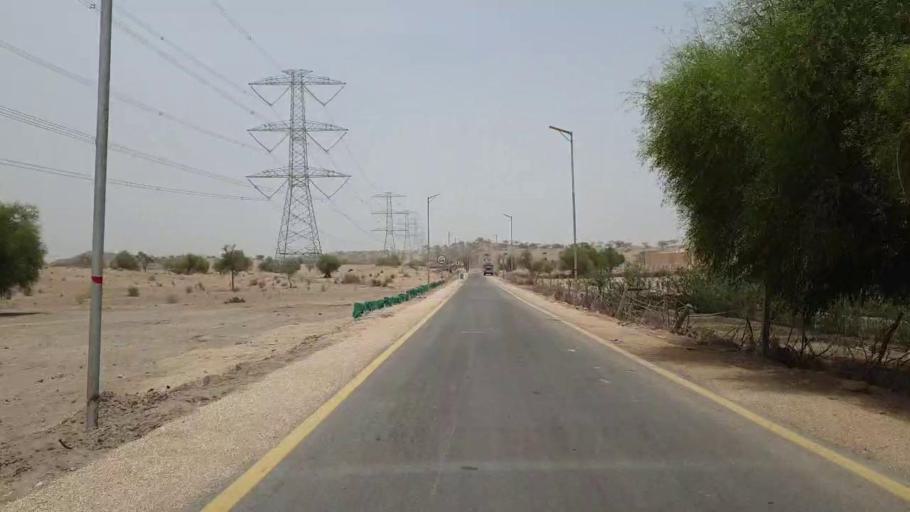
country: PK
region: Sindh
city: Islamkot
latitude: 24.7270
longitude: 70.3213
